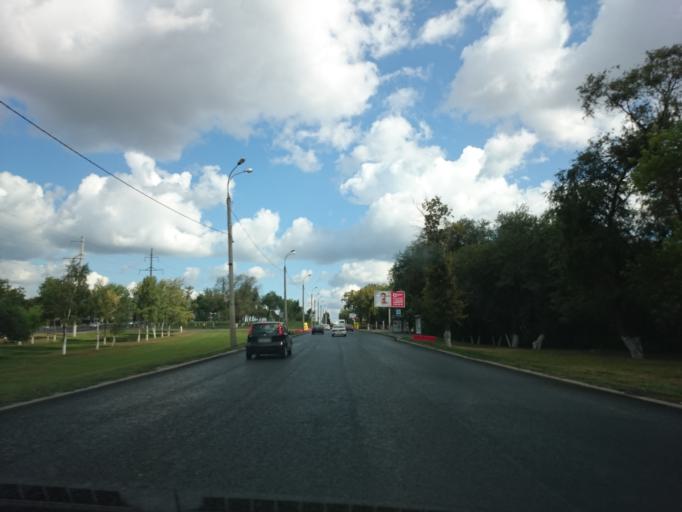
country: RU
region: Samara
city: Samara
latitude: 53.2260
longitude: 50.1735
